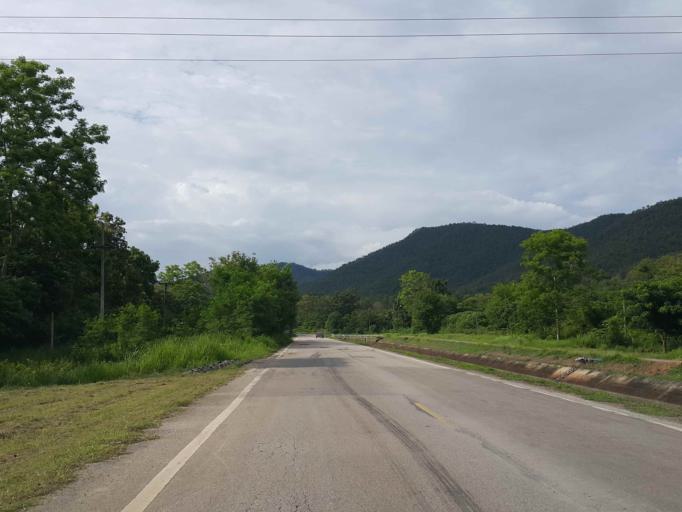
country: TH
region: Chiang Mai
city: San Sai
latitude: 18.9108
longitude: 99.1489
